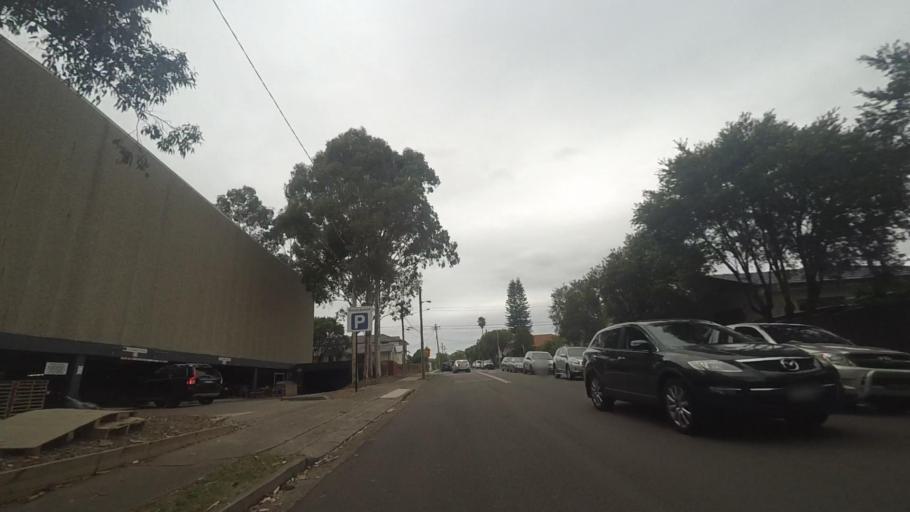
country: AU
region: New South Wales
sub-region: Auburn
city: Auburn
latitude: -33.8408
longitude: 151.0324
